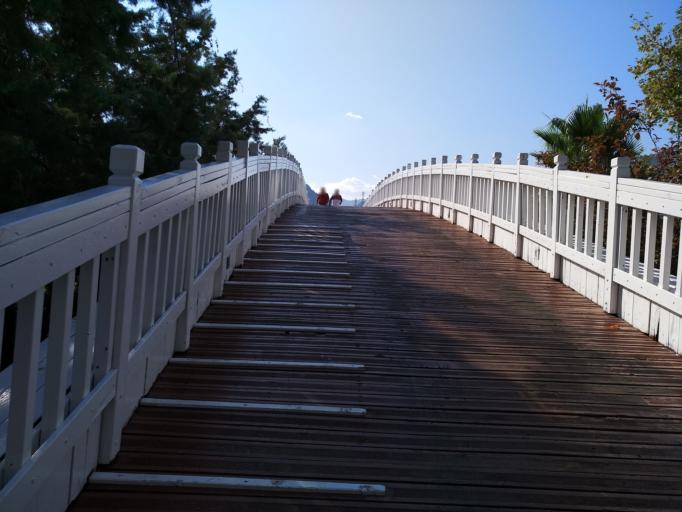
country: TR
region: Antalya
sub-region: Kemer
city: Goeynuek
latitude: 36.6657
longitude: 30.5617
